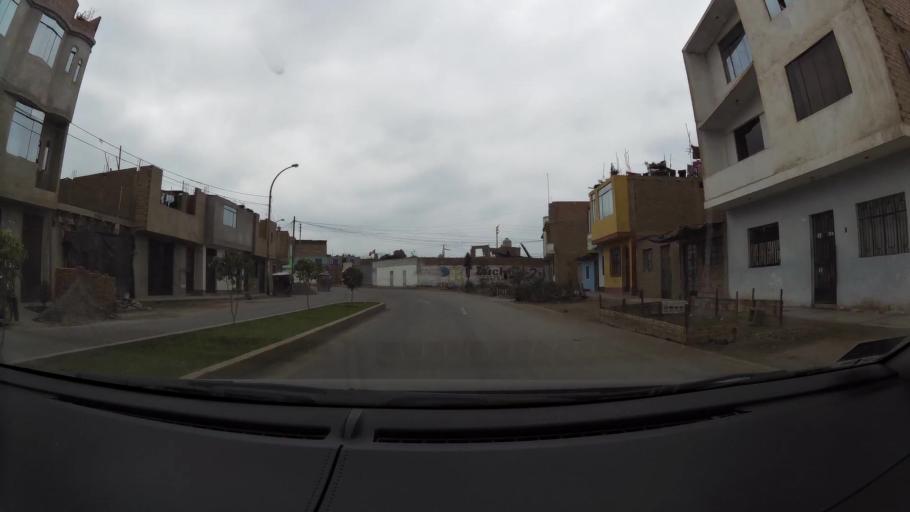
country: PE
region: Lima
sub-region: Provincia de Huaral
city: Huaral
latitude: -11.4987
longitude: -77.1991
